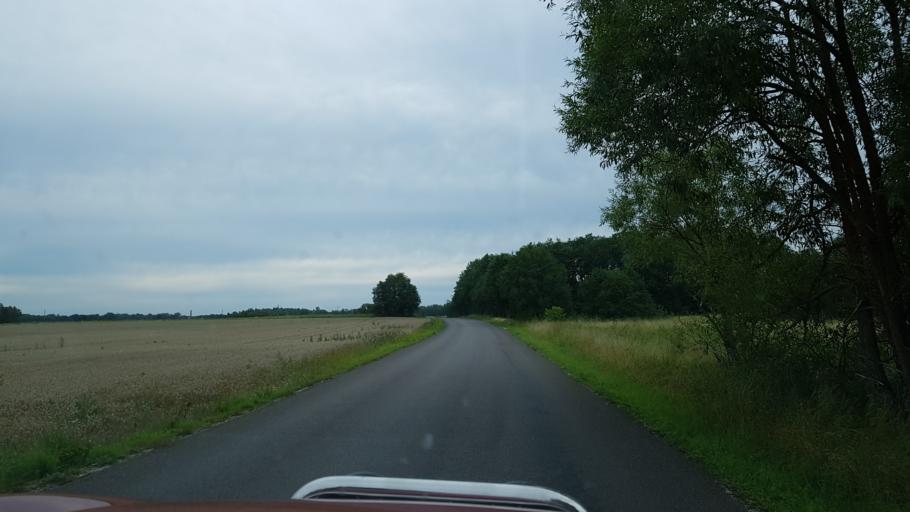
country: EE
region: Laeaene
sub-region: Lihula vald
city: Lihula
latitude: 58.8701
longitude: 23.8042
